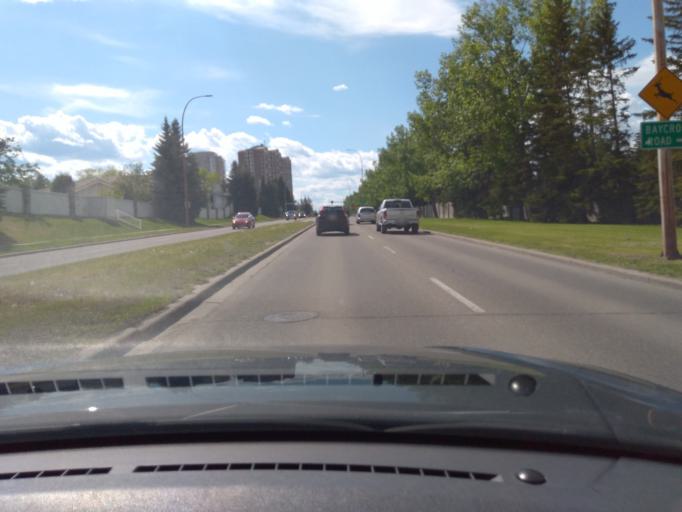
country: CA
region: Alberta
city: Calgary
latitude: 50.9723
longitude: -114.1032
